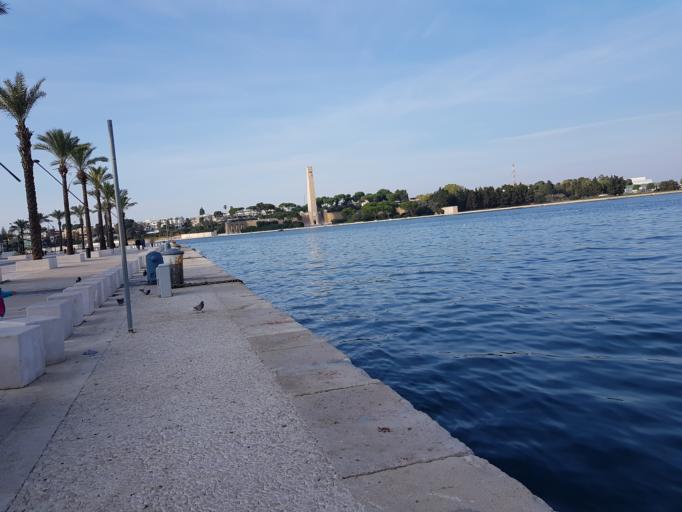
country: IT
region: Apulia
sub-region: Provincia di Brindisi
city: Brindisi
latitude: 40.6404
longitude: 17.9484
